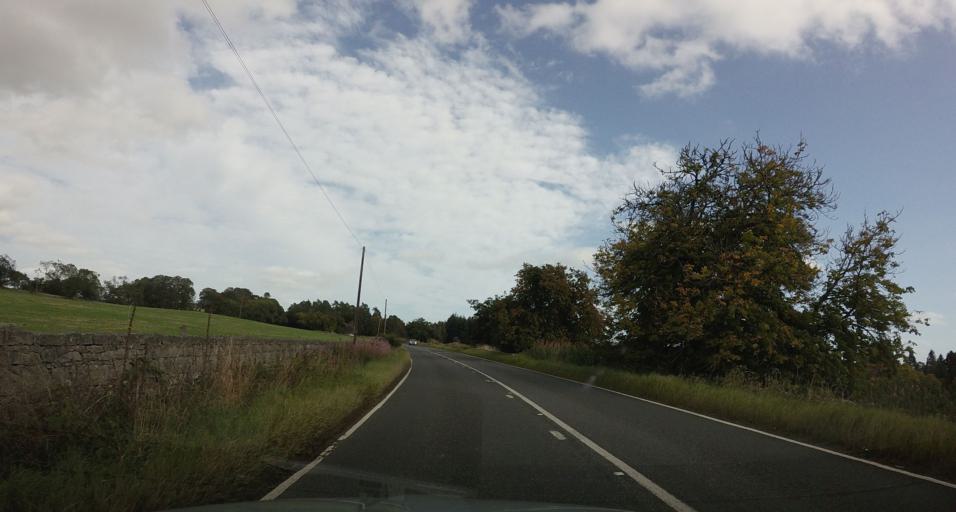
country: GB
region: Scotland
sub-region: Aberdeenshire
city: Kintore
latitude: 57.1640
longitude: -2.3718
